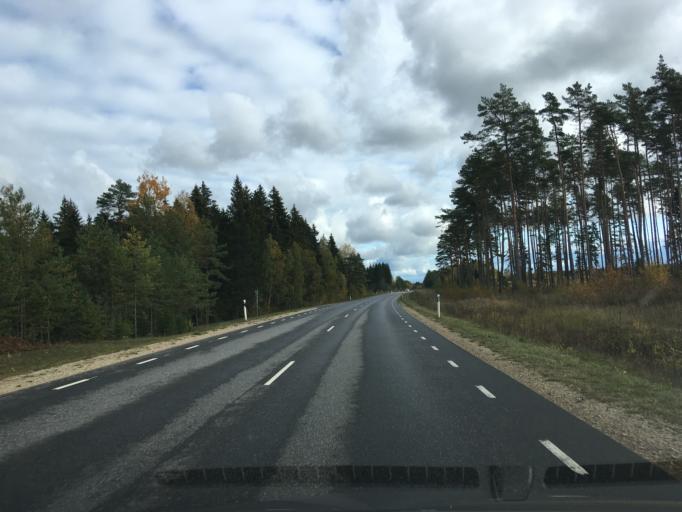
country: EE
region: Harju
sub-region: Anija vald
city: Kehra
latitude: 59.2211
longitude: 25.2455
